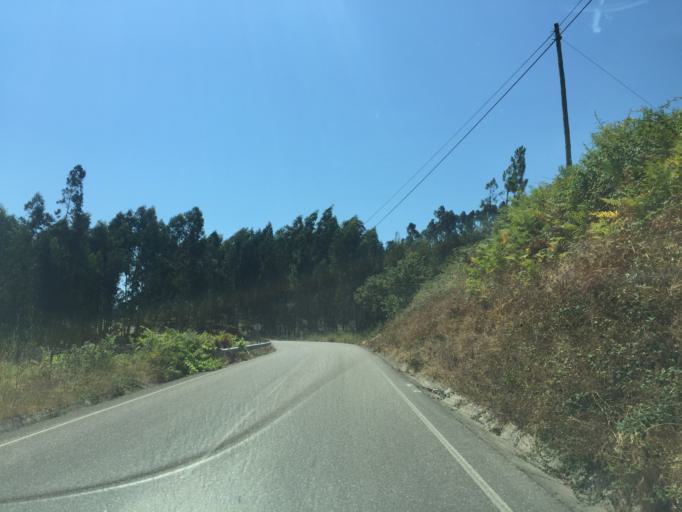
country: PT
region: Santarem
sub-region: Ferreira do Zezere
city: Ferreira do Zezere
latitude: 39.6093
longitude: -8.3111
